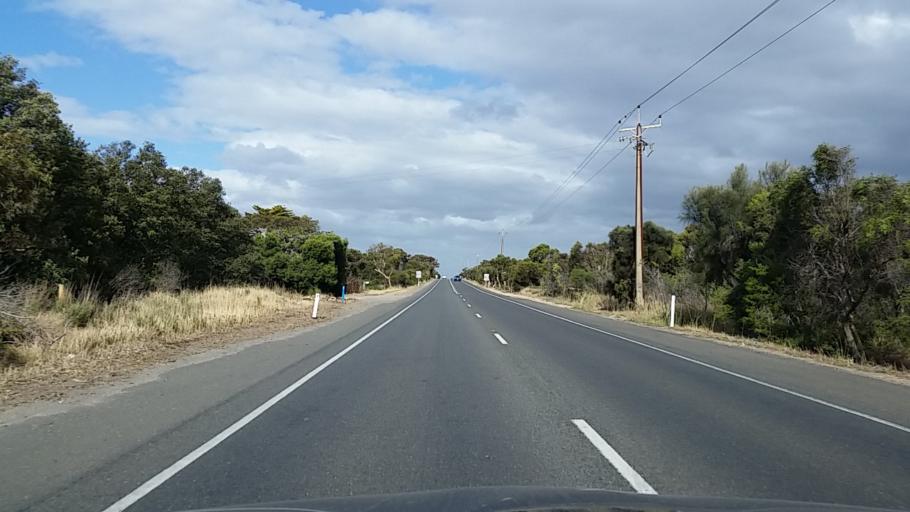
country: AU
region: South Australia
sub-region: Alexandrina
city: Goolwa
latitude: -35.5059
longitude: 138.7623
